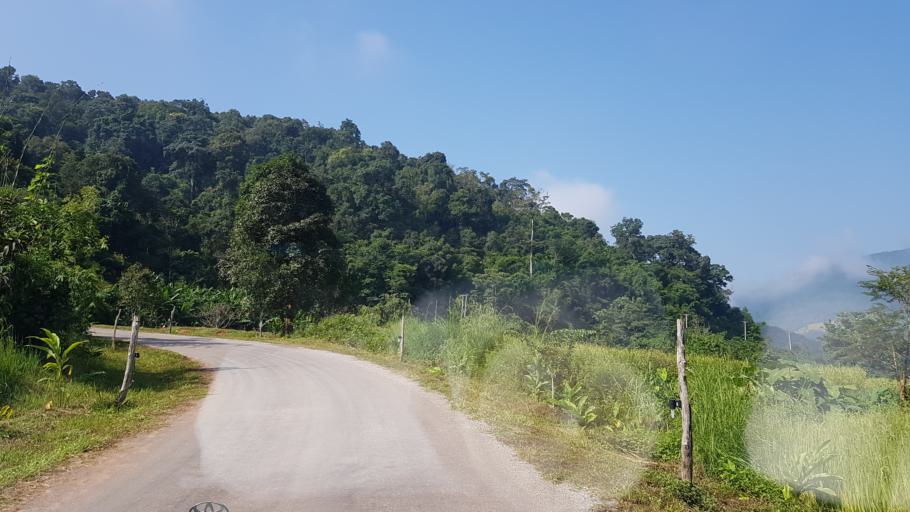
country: LA
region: Oudomxai
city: Muang Xay
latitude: 20.7152
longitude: 102.0960
